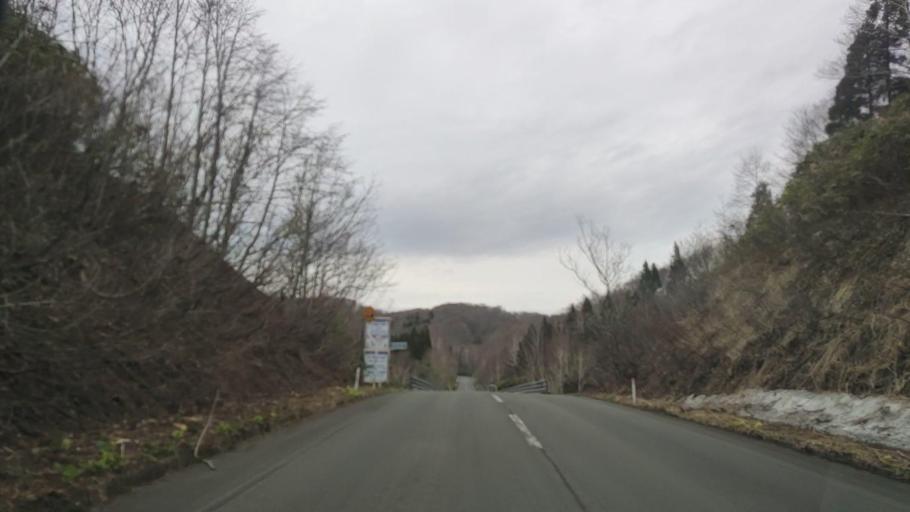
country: JP
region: Akita
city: Hanawa
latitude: 40.4126
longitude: 140.8463
